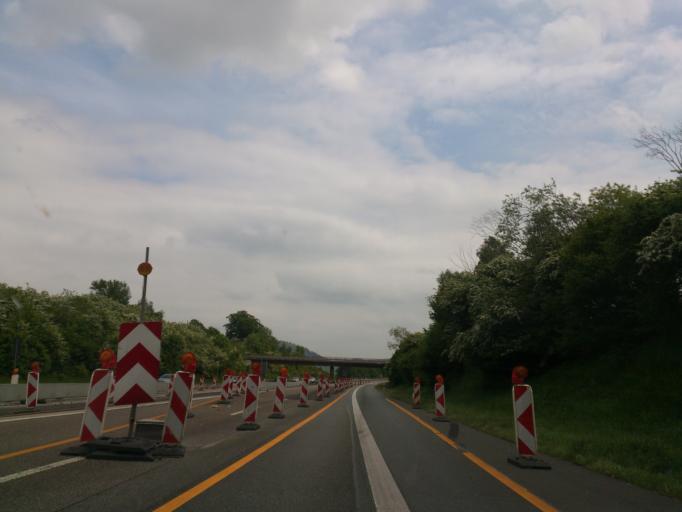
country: DE
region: Hesse
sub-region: Regierungsbezirk Kassel
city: Zierenberg
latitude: 51.3808
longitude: 9.2568
